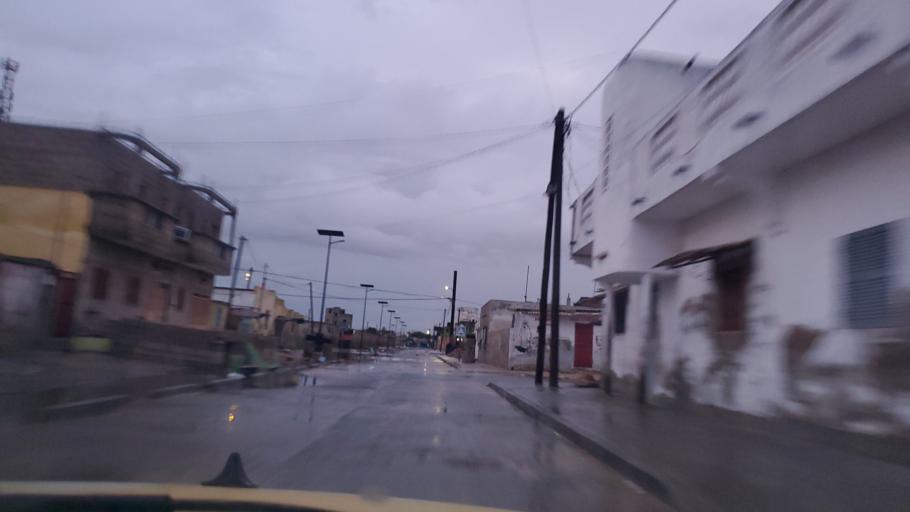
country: SN
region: Saint-Louis
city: Saint-Louis
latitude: 16.0123
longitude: -16.4930
